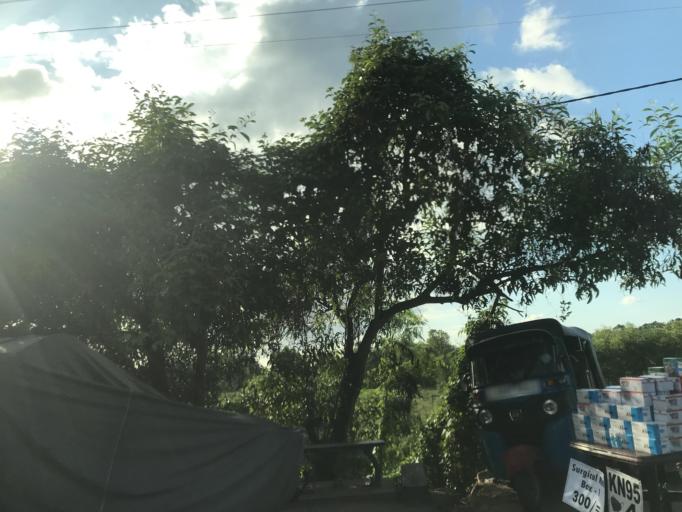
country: LK
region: Western
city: Gampaha
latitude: 7.0940
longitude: 79.9905
